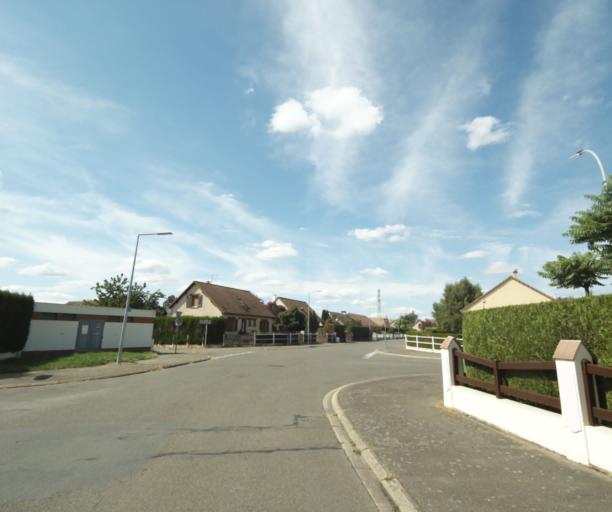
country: FR
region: Centre
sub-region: Departement d'Eure-et-Loir
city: Luce
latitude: 48.4294
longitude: 1.4361
